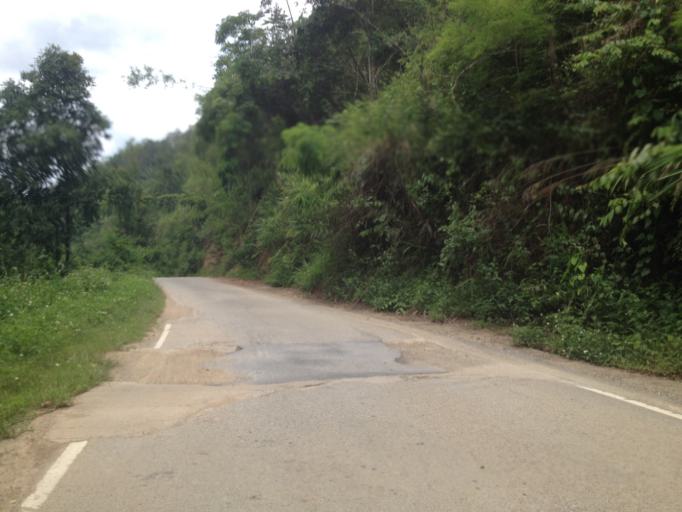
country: TH
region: Chiang Mai
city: Hang Dong
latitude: 18.7192
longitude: 98.8407
